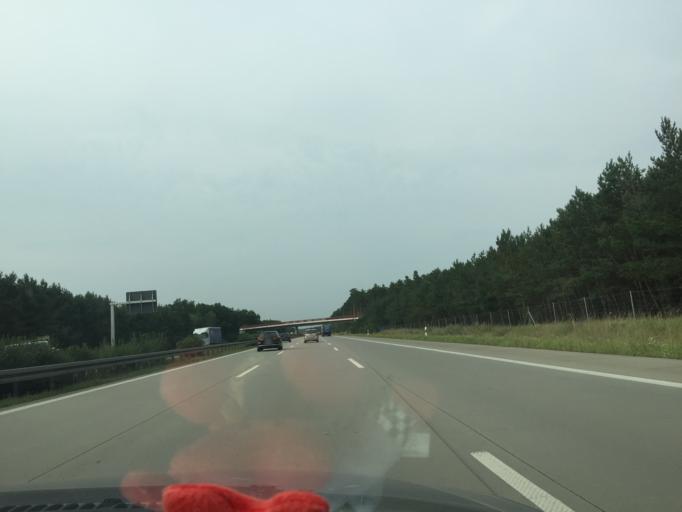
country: DE
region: Brandenburg
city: Grunheide
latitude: 52.3978
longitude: 13.7866
